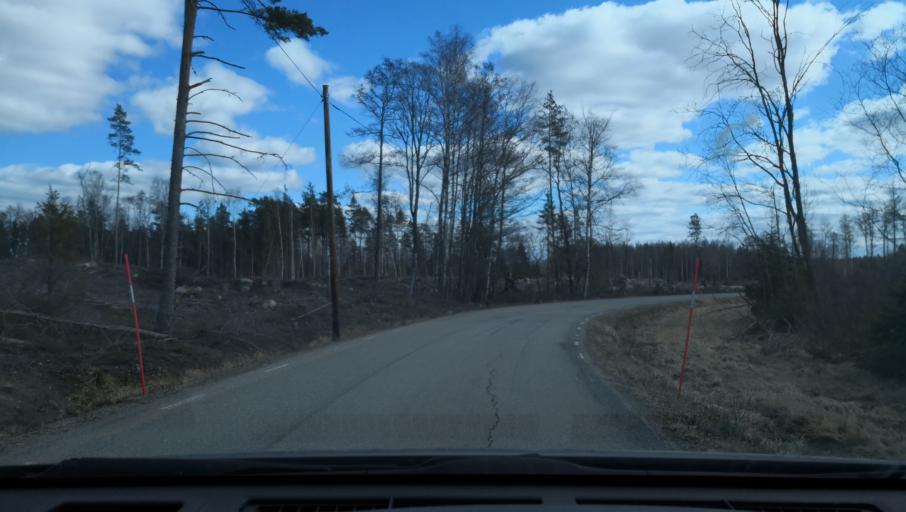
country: SE
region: Vaestmanland
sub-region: Sala Kommun
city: Sala
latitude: 59.8670
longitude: 16.5618
